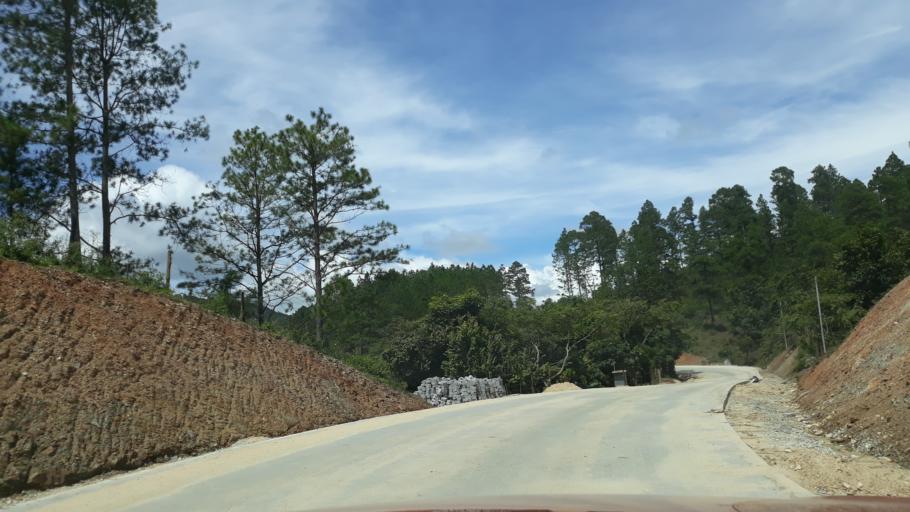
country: HN
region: El Paraiso
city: Santa Cruz
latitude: 13.7569
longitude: -86.6307
